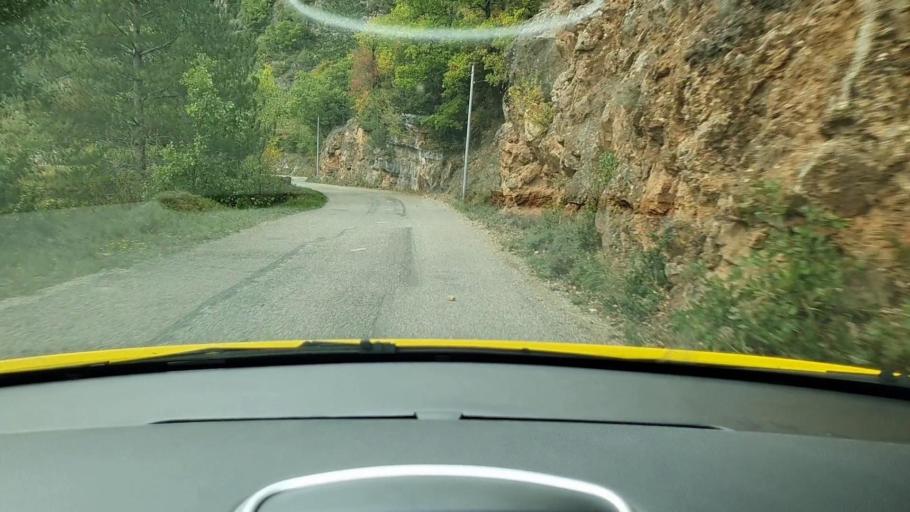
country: FR
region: Languedoc-Roussillon
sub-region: Departement de la Lozere
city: Meyrueis
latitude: 44.0796
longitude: 3.3777
